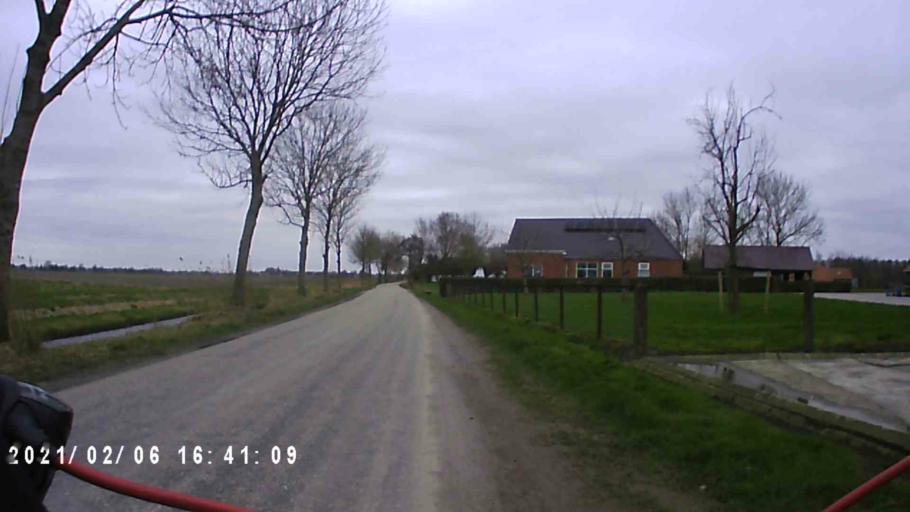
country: NL
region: Groningen
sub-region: Gemeente Bedum
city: Bedum
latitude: 53.4184
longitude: 6.7119
